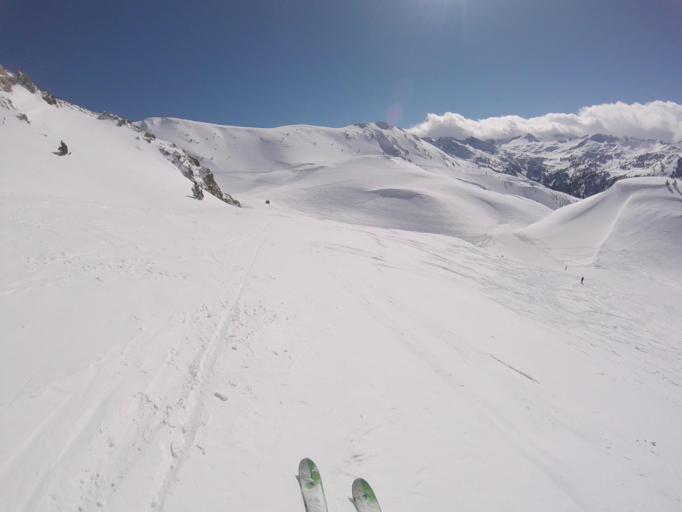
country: ES
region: Catalonia
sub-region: Provincia de Lleida
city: Espot
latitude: 42.6746
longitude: 0.9892
